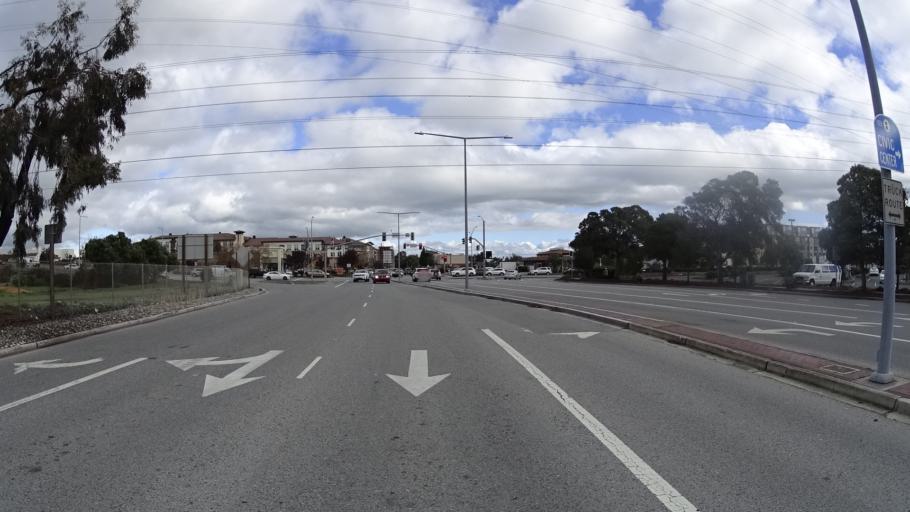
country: US
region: California
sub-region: San Mateo County
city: Foster City
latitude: 37.5622
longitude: -122.2723
